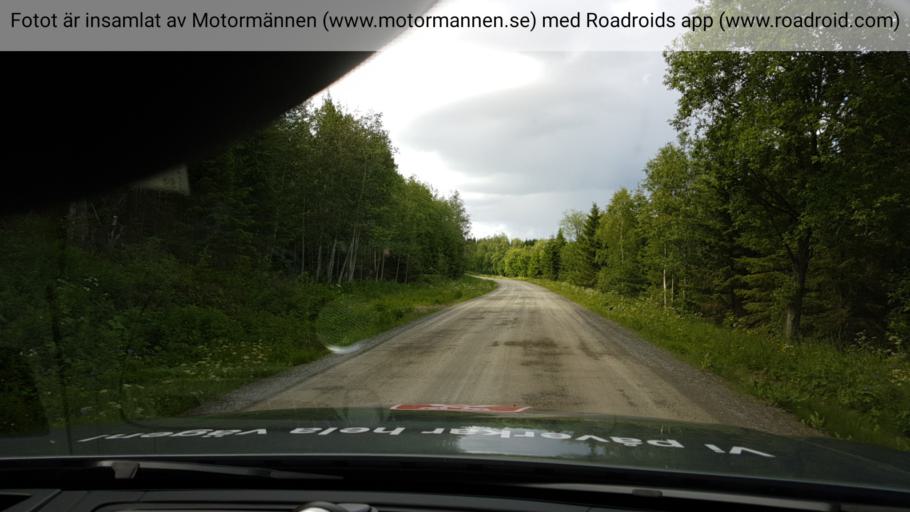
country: SE
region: Jaemtland
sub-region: Bergs Kommun
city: Hoverberg
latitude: 62.9265
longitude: 14.2970
